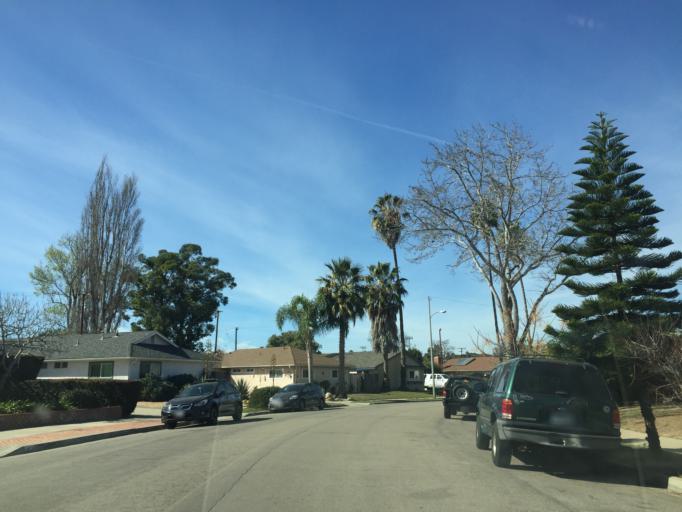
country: US
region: California
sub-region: Santa Barbara County
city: Goleta
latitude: 34.4399
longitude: -119.7829
